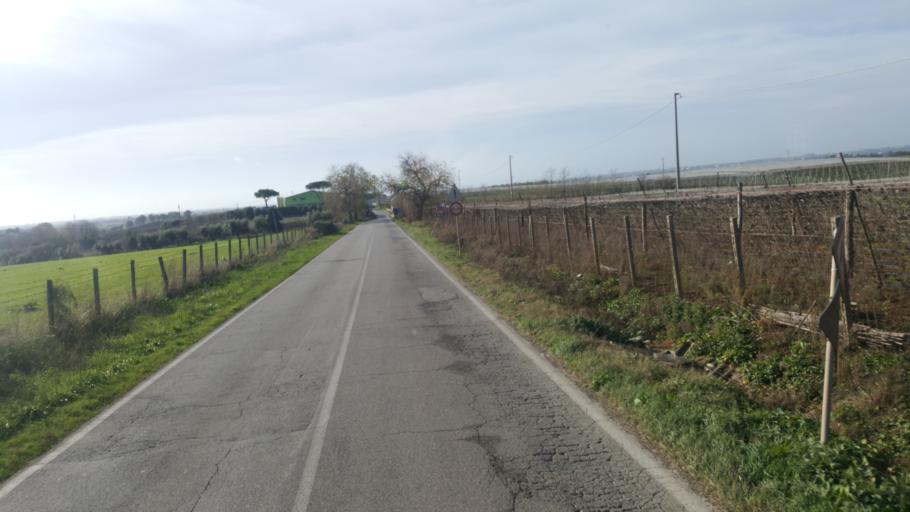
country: IT
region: Latium
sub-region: Citta metropolitana di Roma Capitale
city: Mantiglia di Ardea
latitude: 41.6574
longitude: 12.6261
